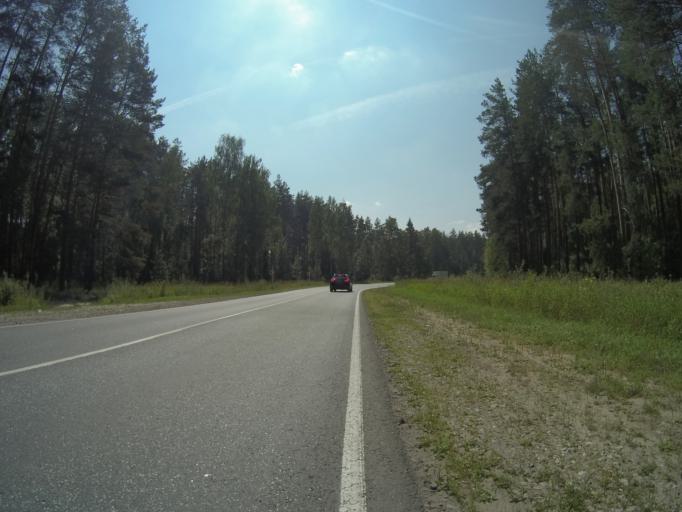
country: RU
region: Vladimir
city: Anopino
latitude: 55.6964
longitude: 40.7495
